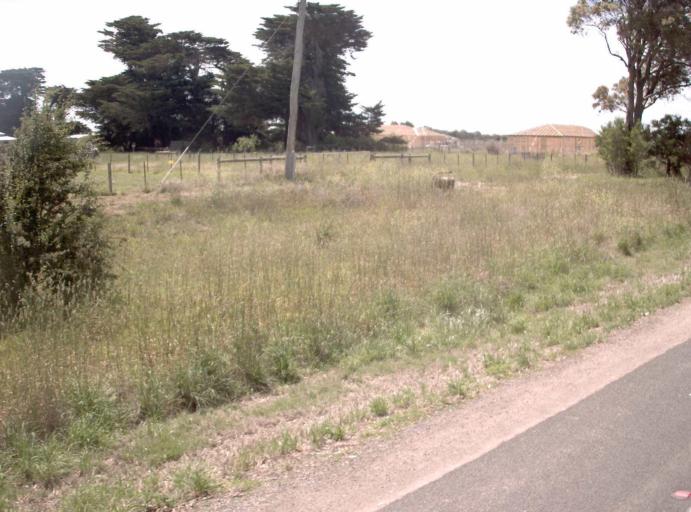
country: AU
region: Victoria
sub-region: Wellington
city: Sale
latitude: -38.0819
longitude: 147.0712
